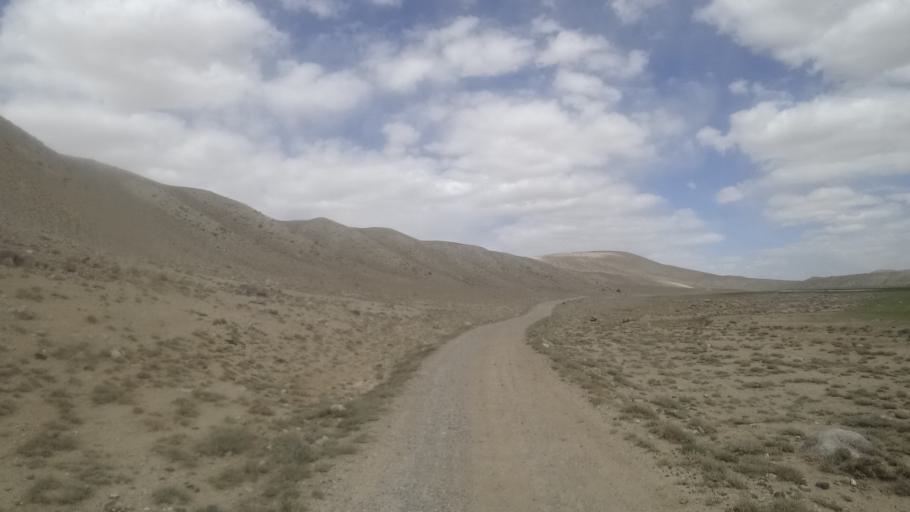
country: AF
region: Badakhshan
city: Khandud
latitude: 37.4066
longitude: 73.1501
